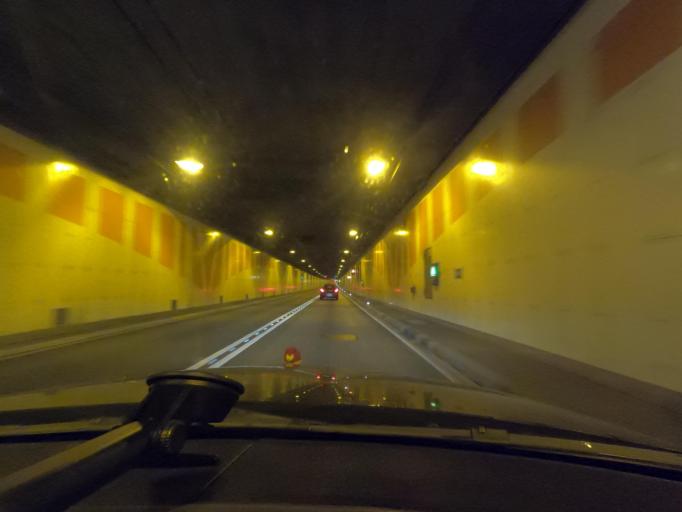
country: DE
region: Hamburg
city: Altona
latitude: 53.5334
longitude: 9.9304
